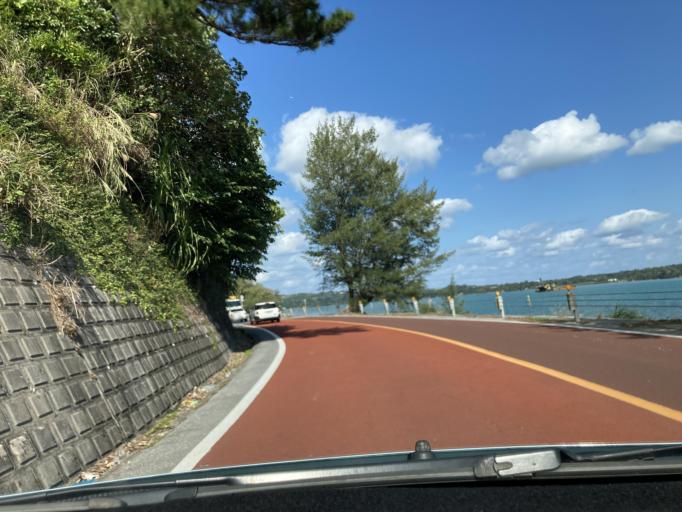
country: JP
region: Okinawa
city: Nago
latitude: 26.6376
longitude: 128.0036
